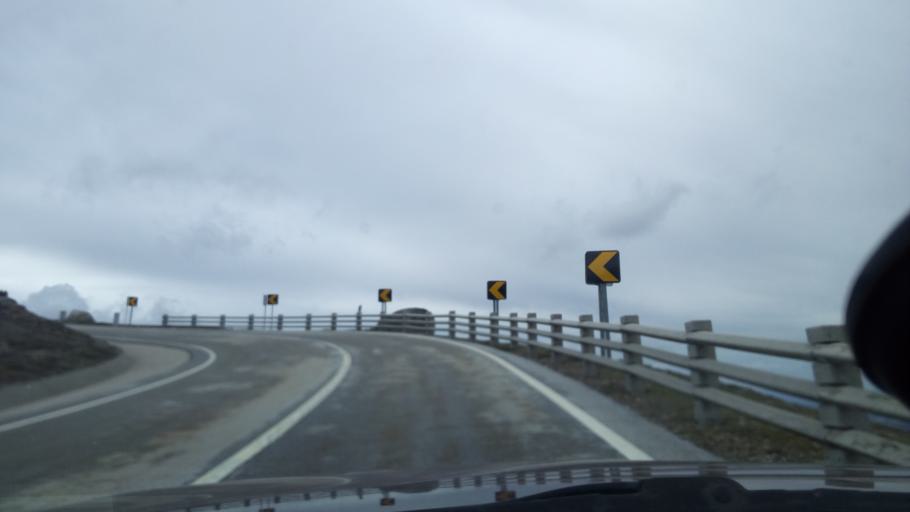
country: PT
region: Guarda
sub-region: Seia
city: Seia
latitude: 40.3444
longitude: -7.6984
